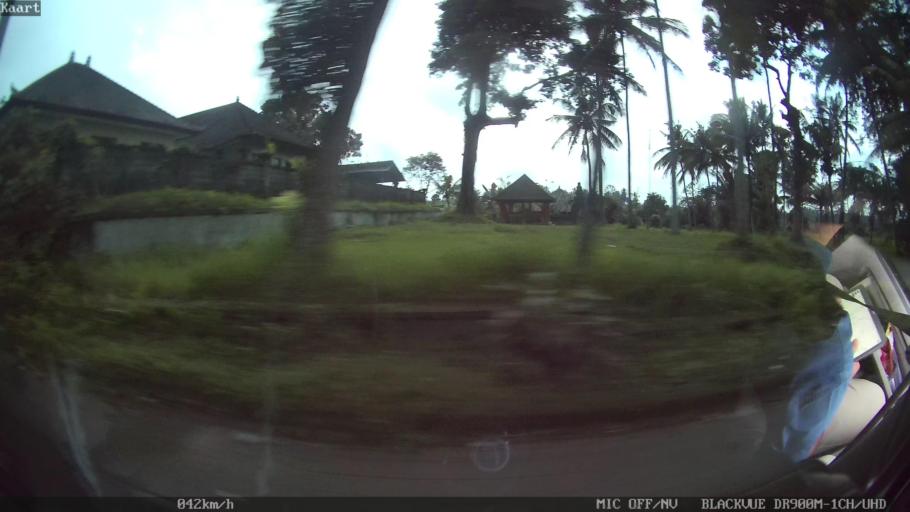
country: ID
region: Bali
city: Bunutan
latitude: -8.4652
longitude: 115.2478
